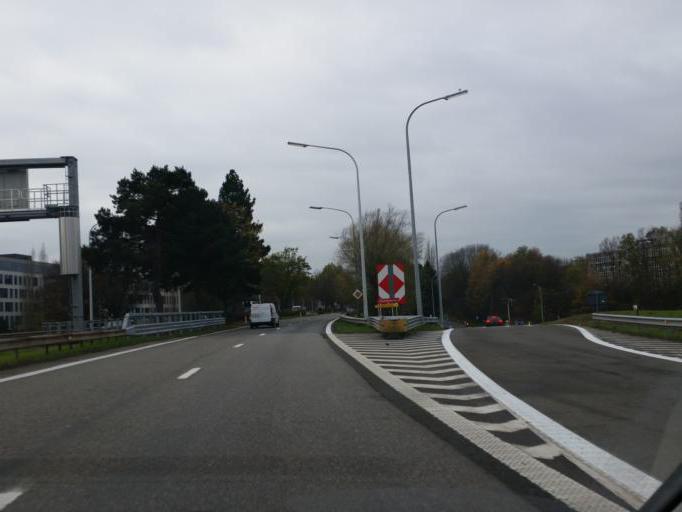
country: BE
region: Flanders
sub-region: Provincie Vlaams-Brabant
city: Diegem
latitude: 50.8851
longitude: 4.4489
